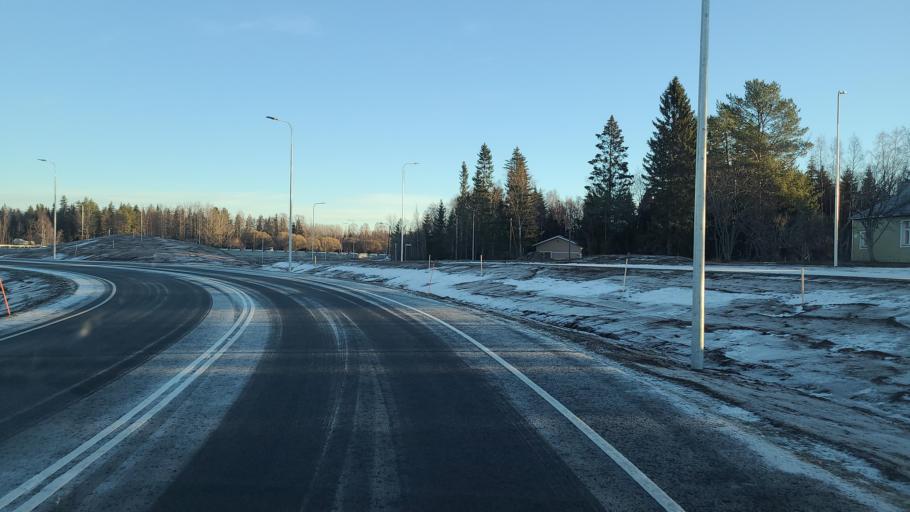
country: FI
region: Lapland
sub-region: Kemi-Tornio
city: Kemi
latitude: 65.6775
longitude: 24.7449
